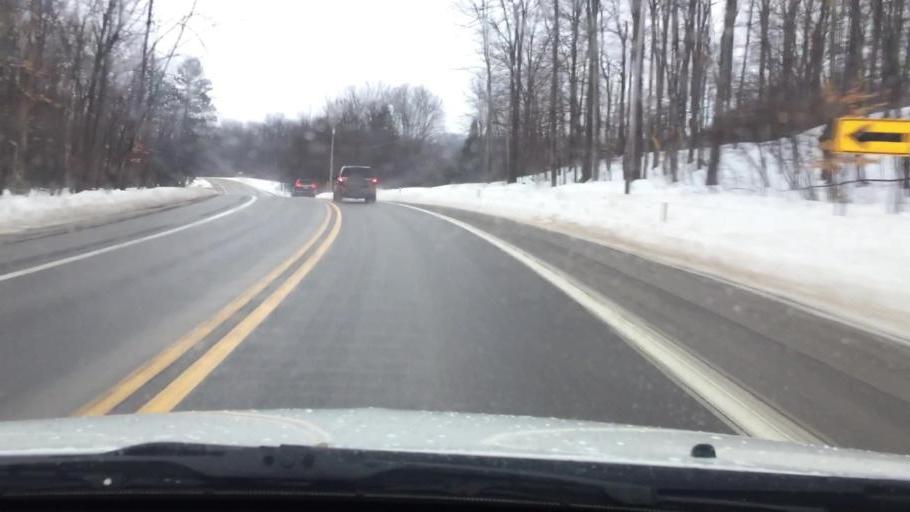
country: US
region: Michigan
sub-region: Charlevoix County
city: East Jordan
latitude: 45.2138
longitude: -85.1720
